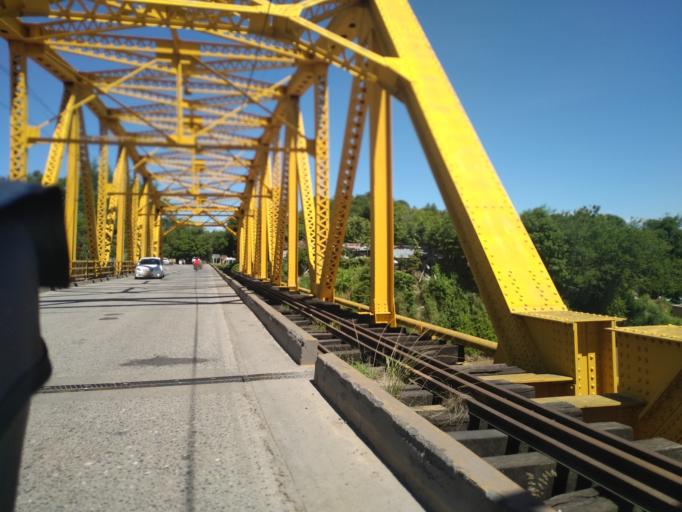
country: CO
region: Cundinamarca
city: Puerto Salgar
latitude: 5.4698
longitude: -74.6642
